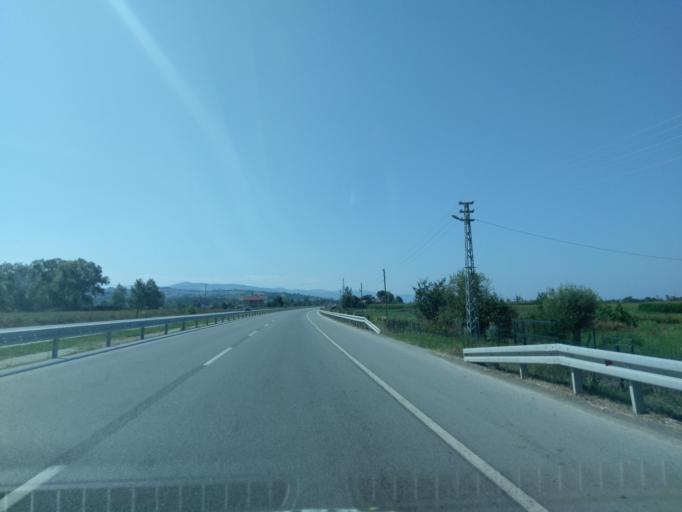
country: TR
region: Samsun
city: Alacam
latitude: 41.6084
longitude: 35.6676
